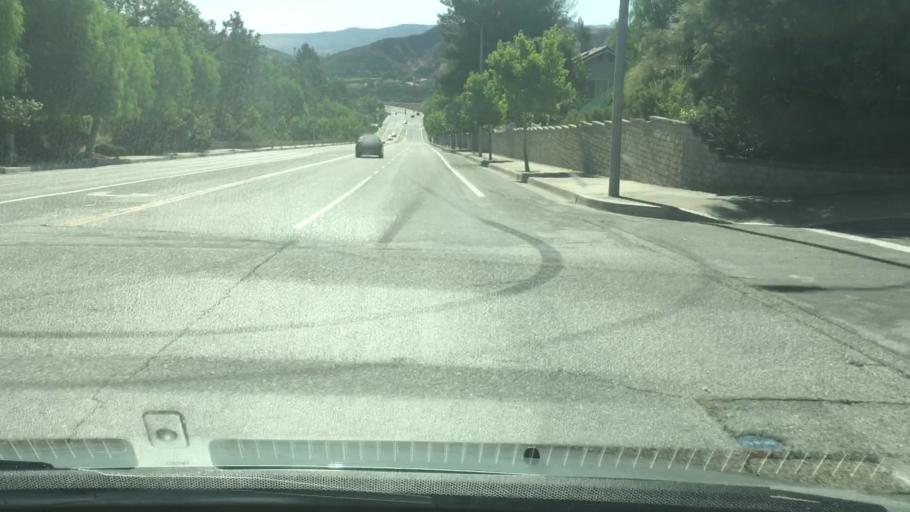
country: US
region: California
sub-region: Los Angeles County
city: Santa Clarita
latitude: 34.4598
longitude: -118.5167
